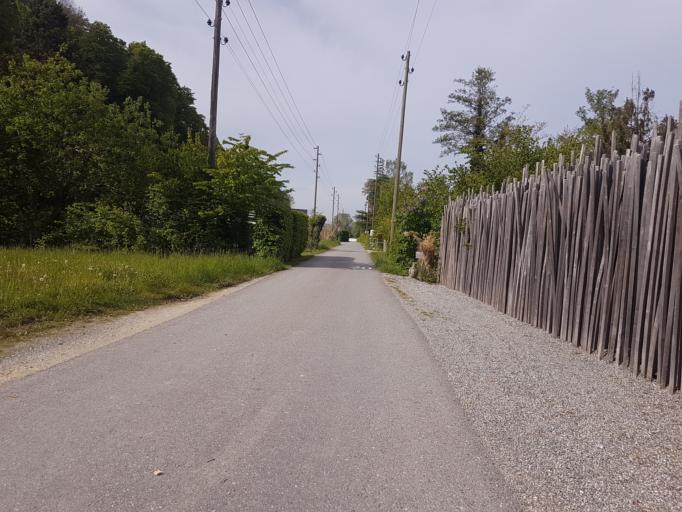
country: CH
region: Bern
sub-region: Seeland District
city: Tauffelen
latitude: 47.0790
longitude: 7.1982
